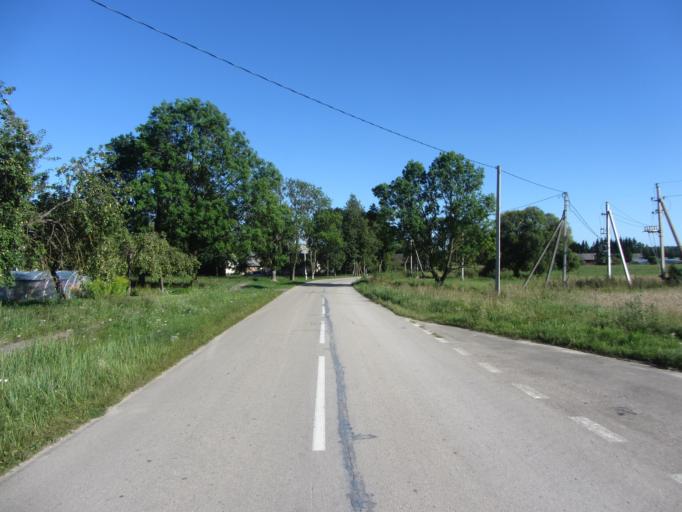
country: LT
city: Obeliai
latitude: 55.7997
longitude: 25.2470
